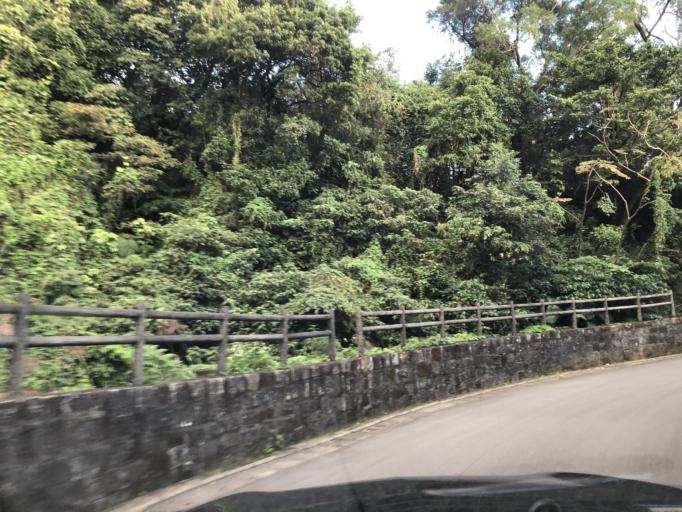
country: TW
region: Taipei
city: Taipei
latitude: 25.1524
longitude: 121.5585
